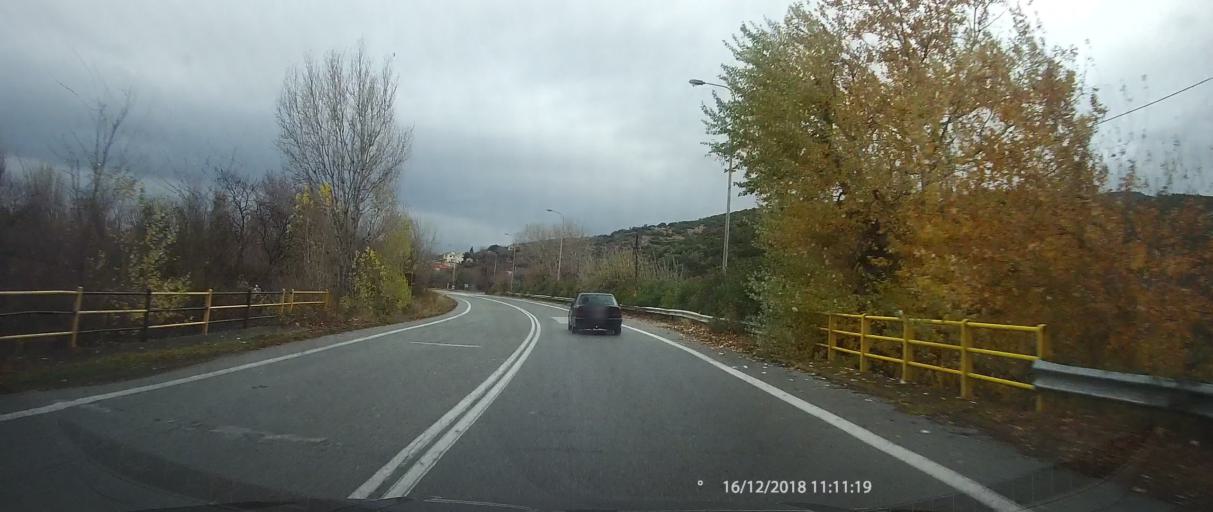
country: GR
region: East Macedonia and Thrace
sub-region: Nomos Xanthis
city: Petrochori
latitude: 41.0865
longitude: 24.7657
